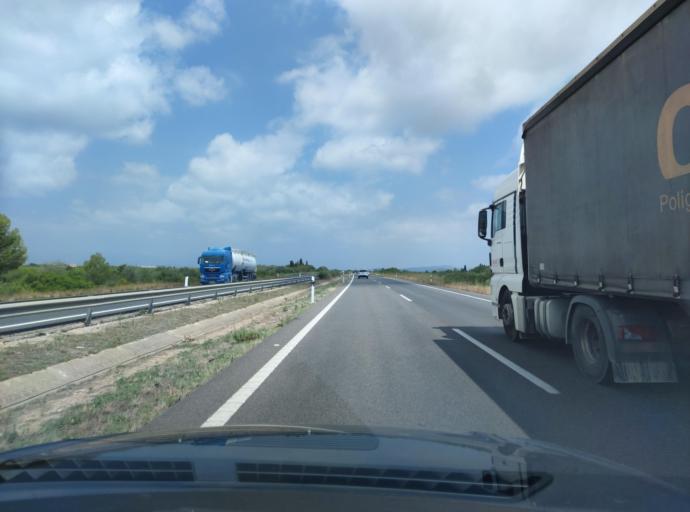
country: ES
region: Valencia
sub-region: Provincia de Castello
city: Vinaros
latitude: 40.5044
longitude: 0.4160
